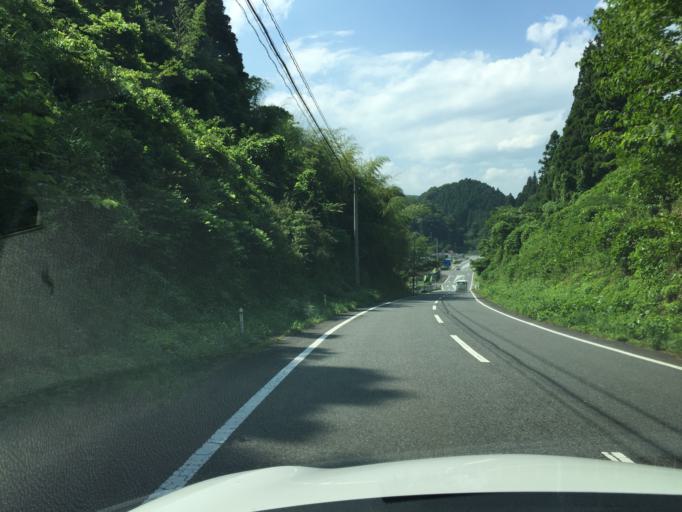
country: JP
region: Ibaraki
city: Kitaibaraki
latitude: 36.9507
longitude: 140.7068
